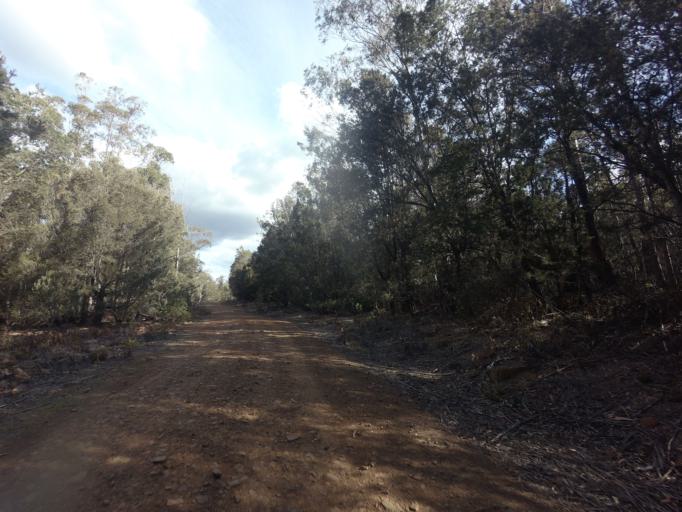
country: AU
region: Tasmania
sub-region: Break O'Day
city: St Helens
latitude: -41.8417
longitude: 148.0867
